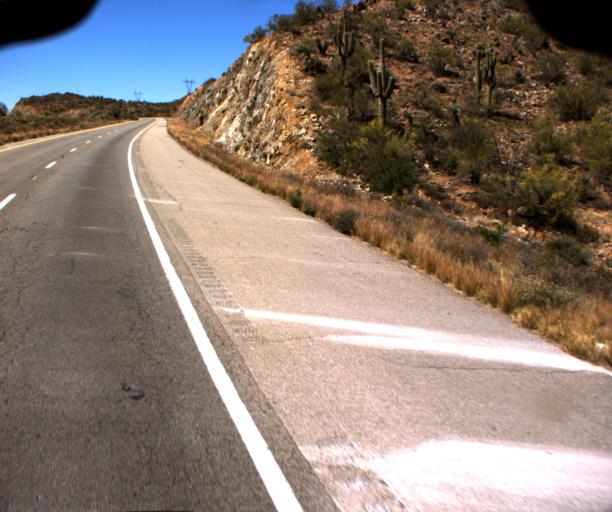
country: US
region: Arizona
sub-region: Yavapai County
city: Bagdad
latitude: 34.4530
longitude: -113.2881
